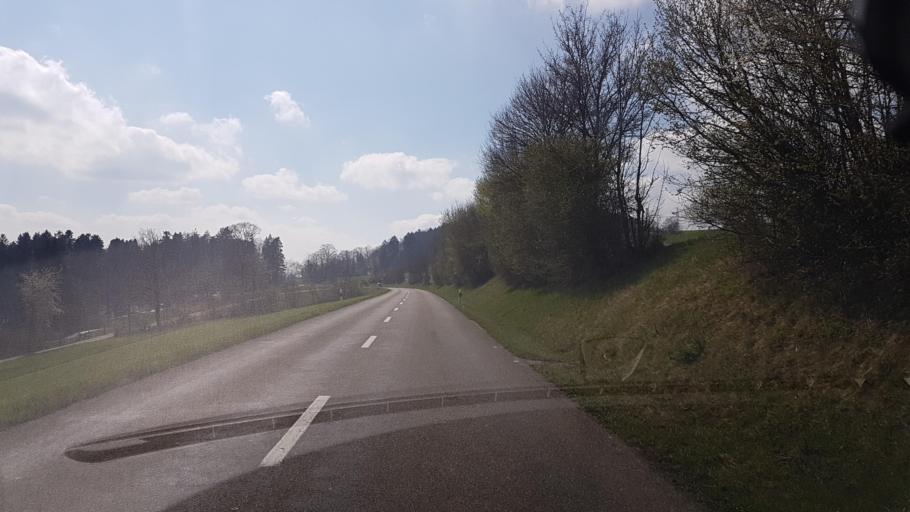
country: CH
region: Aargau
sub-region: Bezirk Bremgarten
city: Rudolfstetten
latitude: 47.3739
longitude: 8.3762
